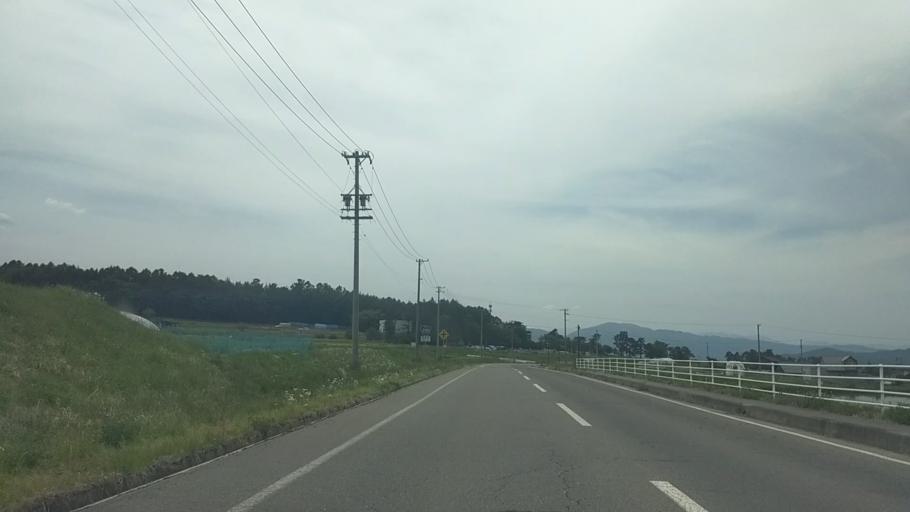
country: JP
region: Nagano
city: Chino
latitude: 36.0259
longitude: 138.2338
